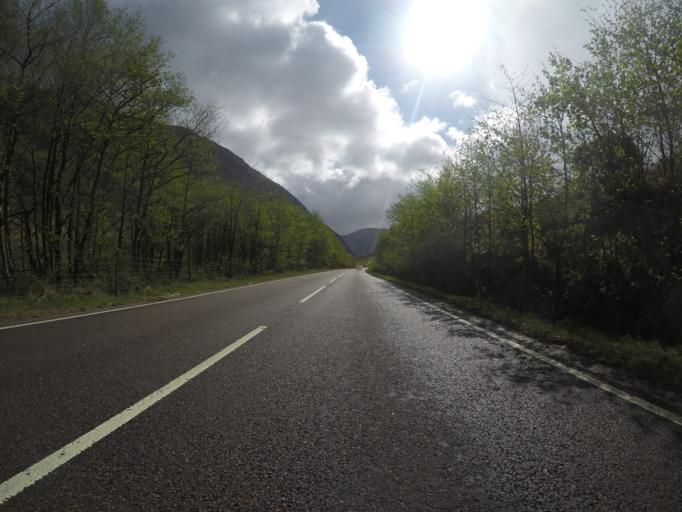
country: GB
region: Scotland
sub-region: Highland
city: Fort William
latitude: 57.1814
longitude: -5.3792
